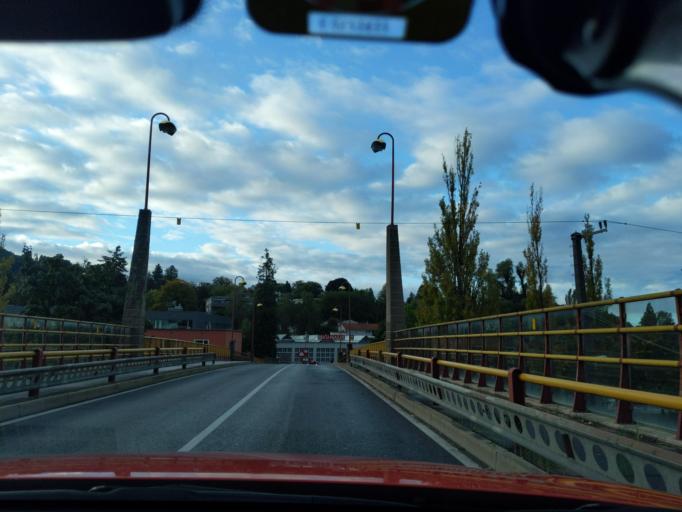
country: AT
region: Vorarlberg
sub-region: Politischer Bezirk Bregenz
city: Bregenz
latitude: 47.5023
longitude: 9.7370
